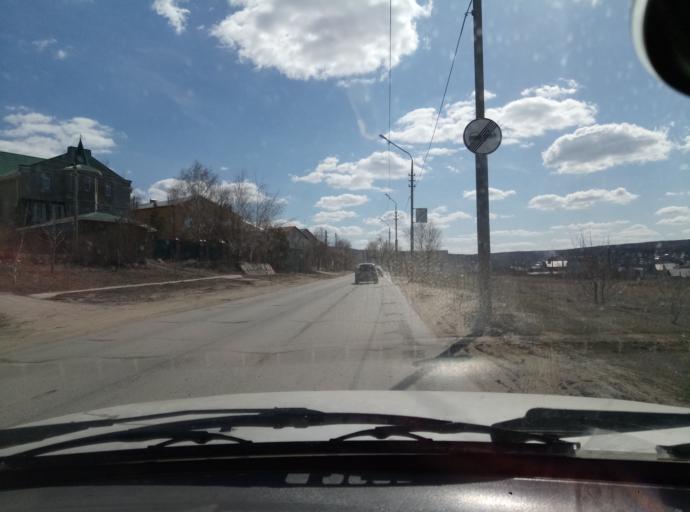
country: RU
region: Saratov
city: Sokolovyy
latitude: 51.5807
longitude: 45.8991
